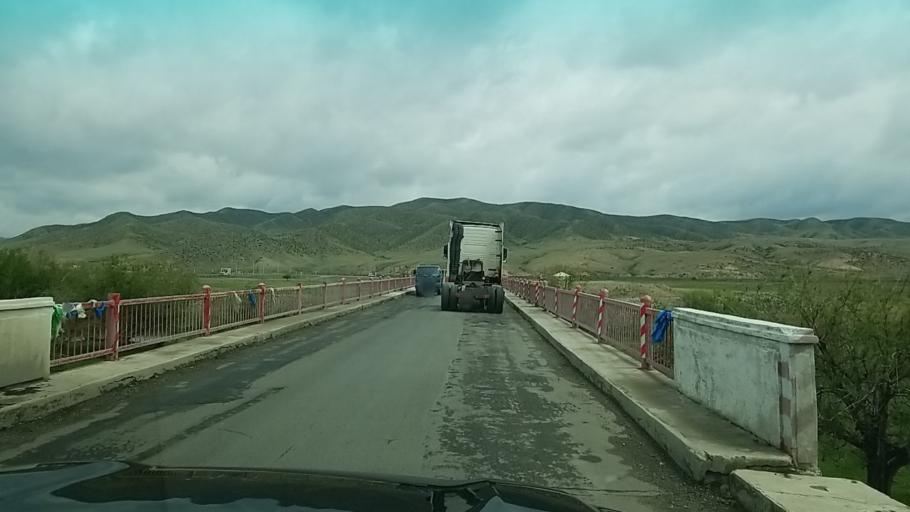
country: MN
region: Central Aimak
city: Javhlant
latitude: 48.8873
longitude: 106.0974
